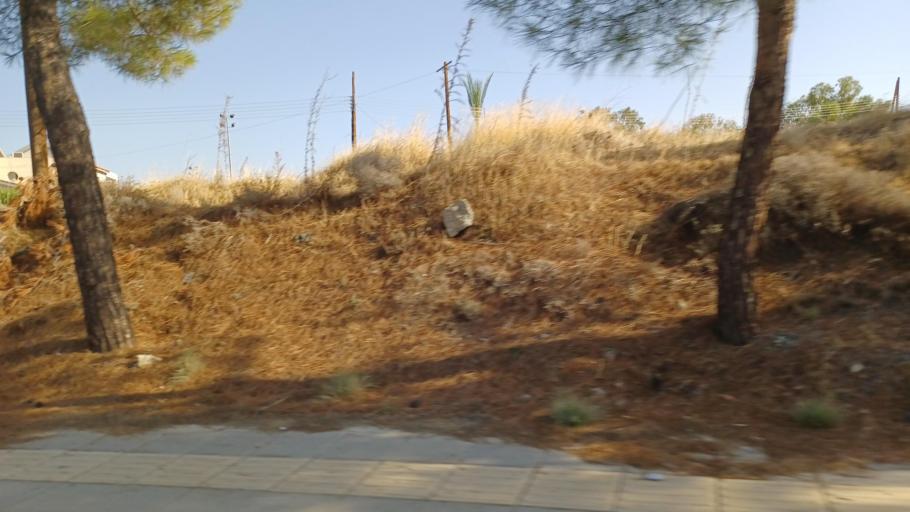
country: CY
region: Lefkosia
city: Lythrodontas
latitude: 34.9495
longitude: 33.3037
